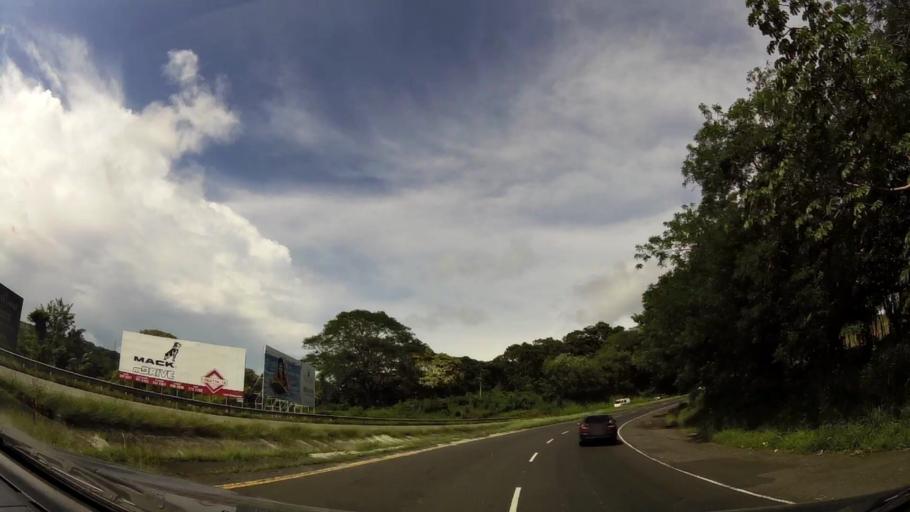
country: PA
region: Panama
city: Capira
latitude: 8.7031
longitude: -79.8723
